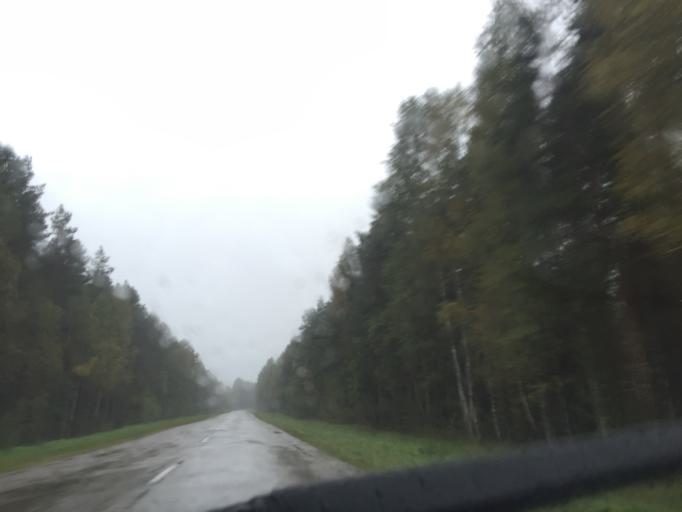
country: LV
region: Ropazu
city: Ropazi
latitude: 57.0035
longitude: 24.6721
